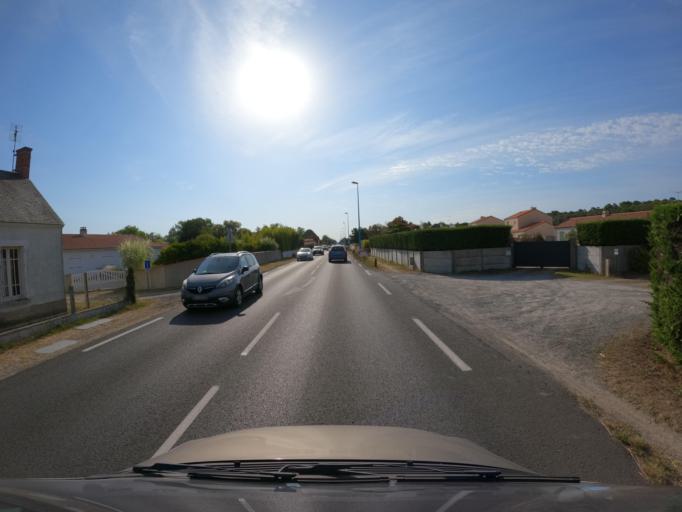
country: FR
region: Pays de la Loire
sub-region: Departement de la Vendee
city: Saint-Jean-de-Monts
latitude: 46.8024
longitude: -2.0856
